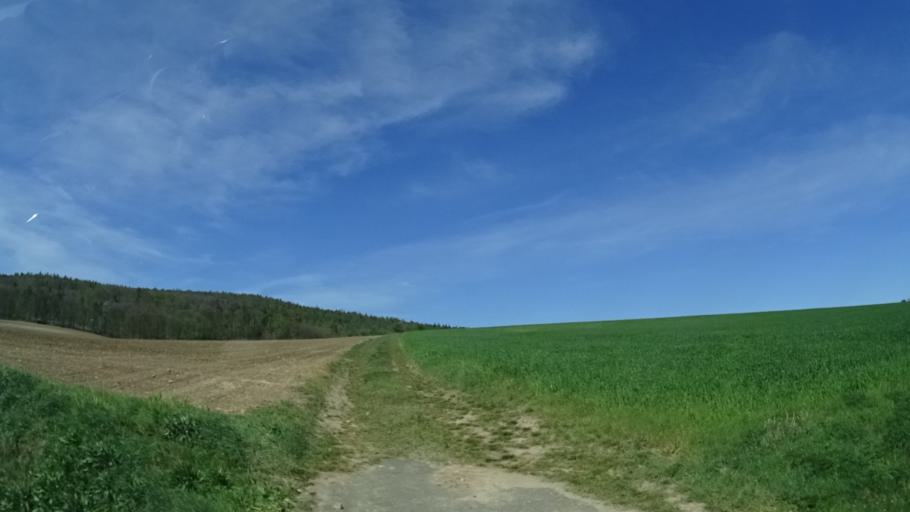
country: DE
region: Bavaria
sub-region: Regierungsbezirk Unterfranken
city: Burgpreppach
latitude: 50.1538
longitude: 10.6244
